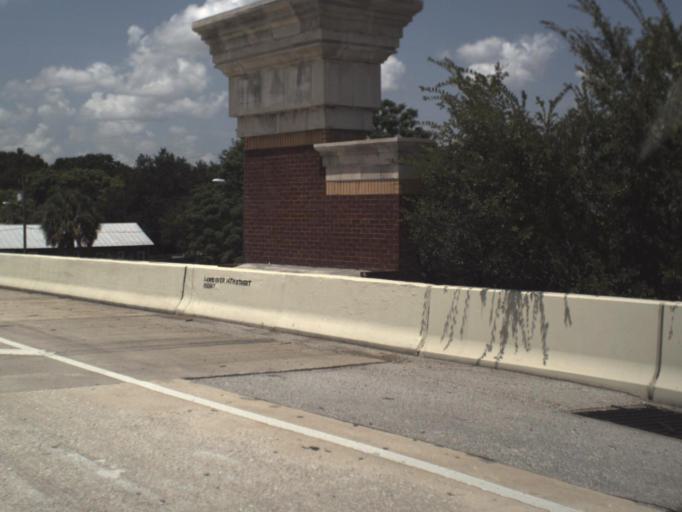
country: US
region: Florida
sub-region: Hillsborough County
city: Tampa
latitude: 27.9650
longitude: -82.4439
